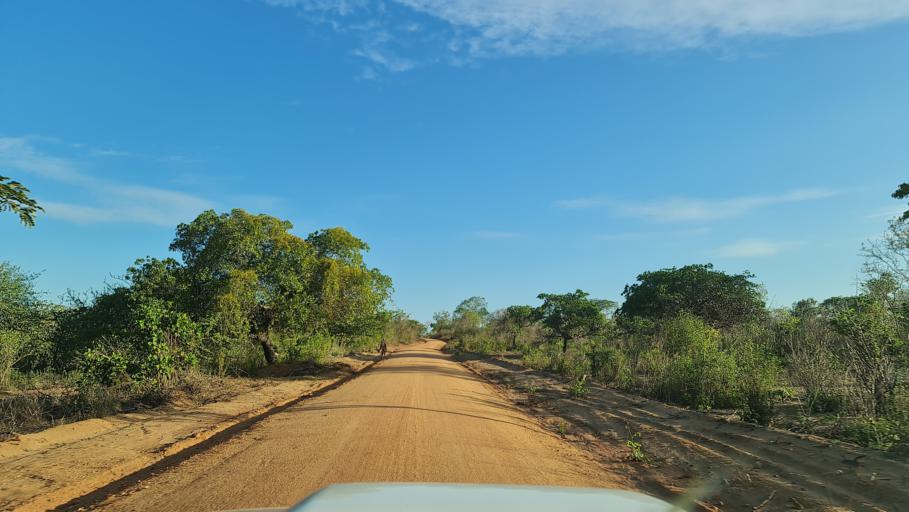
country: MZ
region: Nampula
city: Nacala
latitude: -14.6892
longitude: 40.3151
